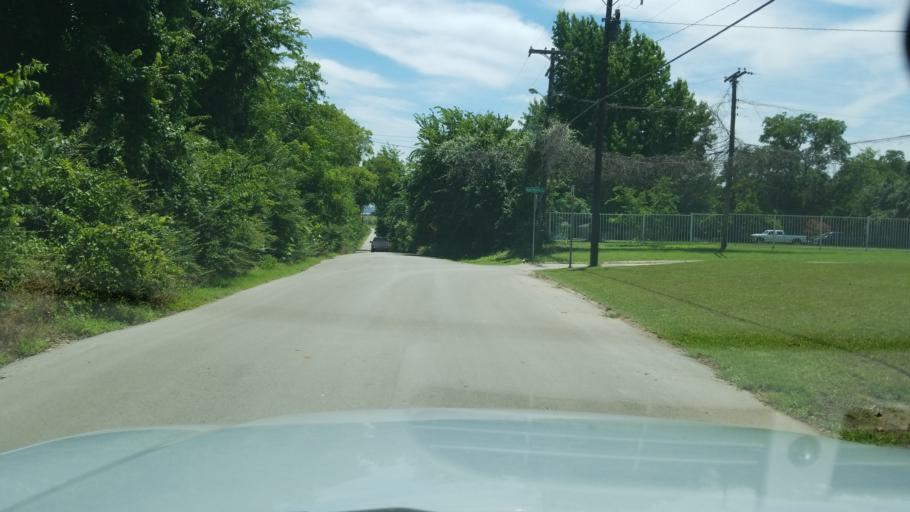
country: US
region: Texas
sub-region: Dallas County
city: Irving
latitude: 32.8084
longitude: -96.9150
